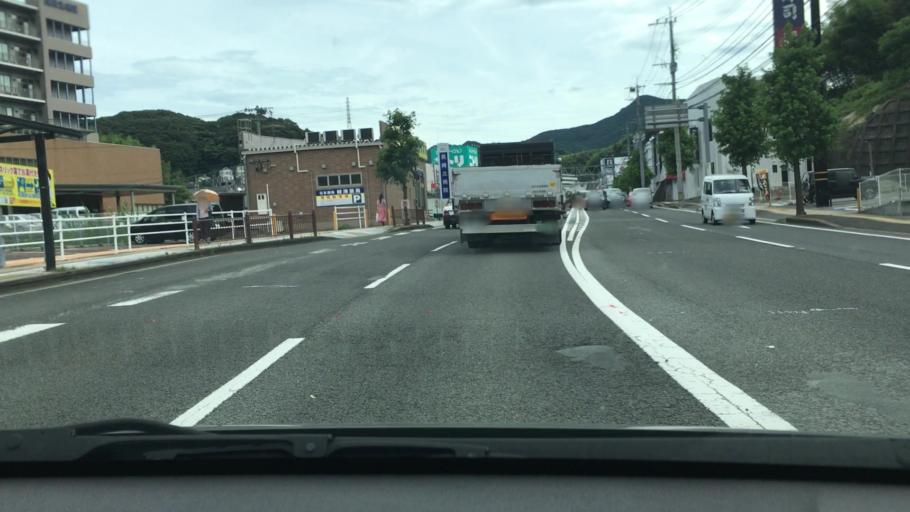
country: JP
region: Nagasaki
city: Togitsu
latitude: 32.8214
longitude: 129.8484
